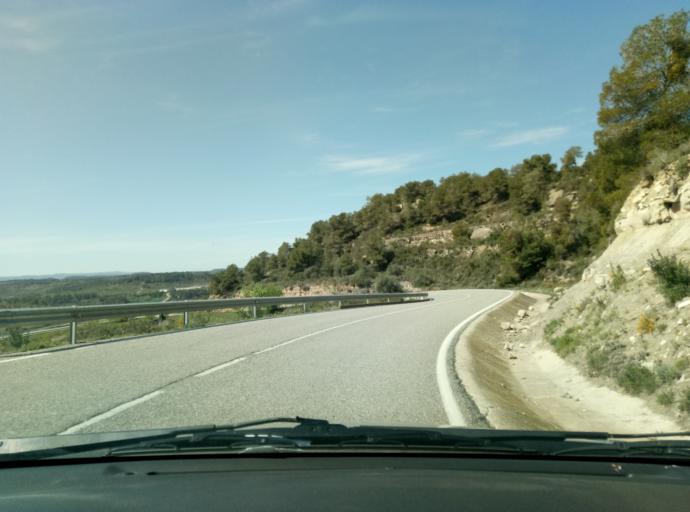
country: ES
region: Catalonia
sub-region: Provincia de Lleida
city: Fulleda
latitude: 41.4998
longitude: 1.0019
